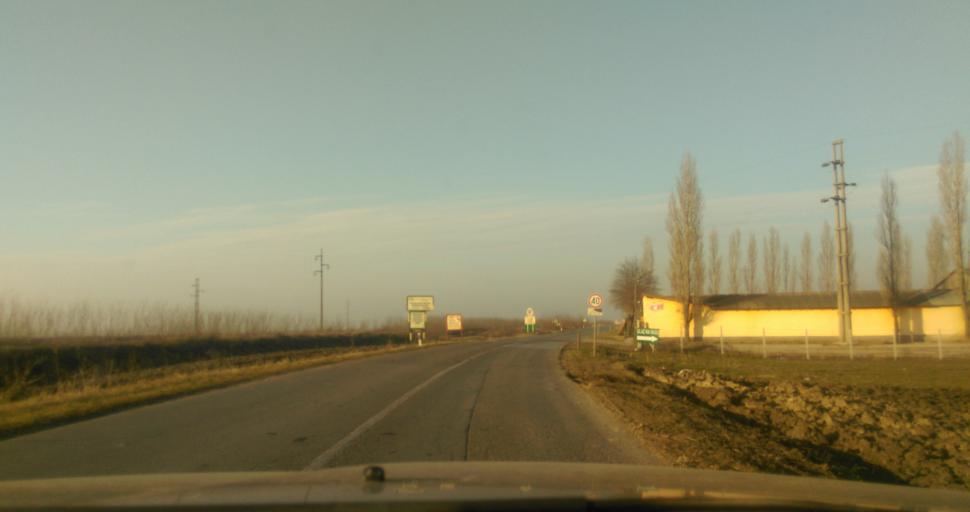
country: RS
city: Curug
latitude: 45.4743
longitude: 20.0443
